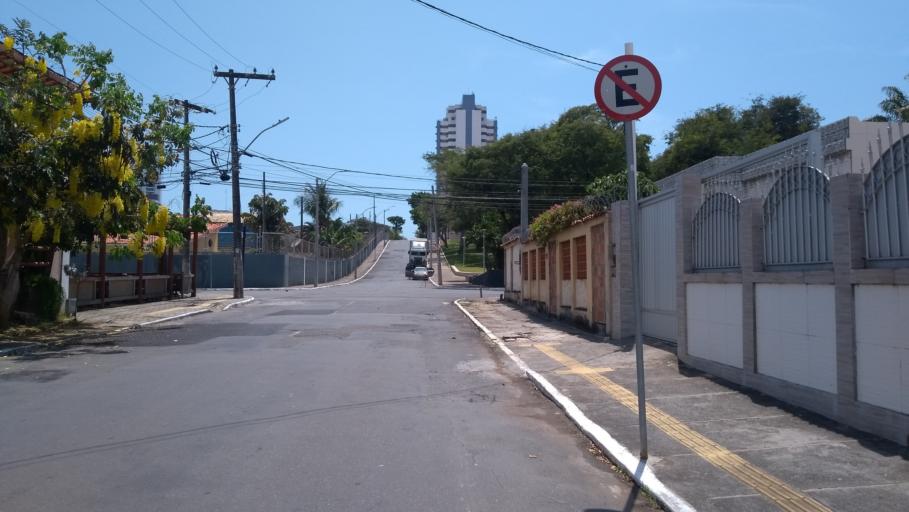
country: BR
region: Bahia
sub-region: Salvador
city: Salvador
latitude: -12.9915
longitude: -38.4596
